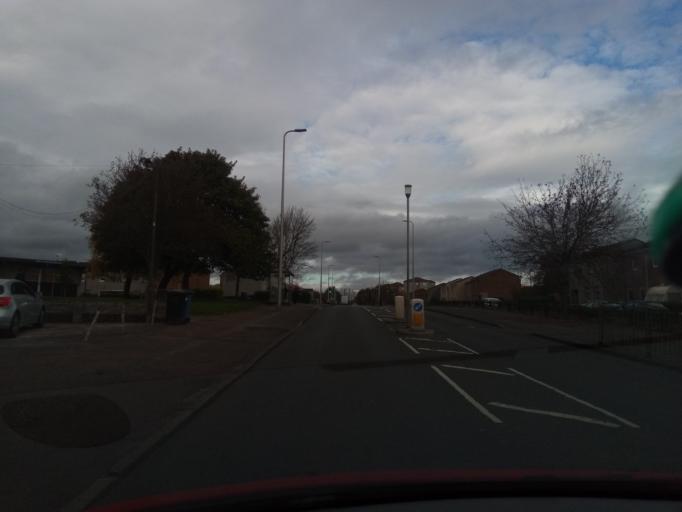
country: GB
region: Scotland
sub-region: West Lothian
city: Blackburn
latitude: 55.8754
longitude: -3.6242
